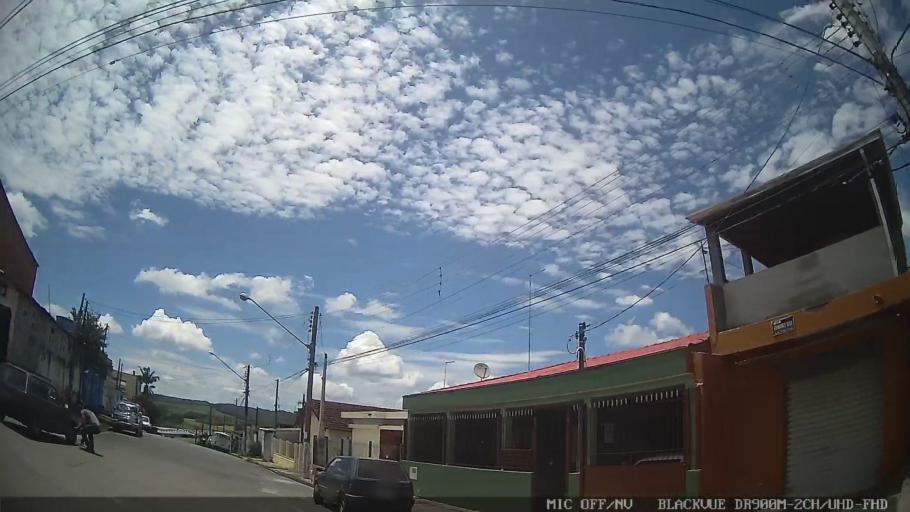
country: BR
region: Sao Paulo
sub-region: Biritiba-Mirim
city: Biritiba Mirim
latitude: -23.5837
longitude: -46.0429
